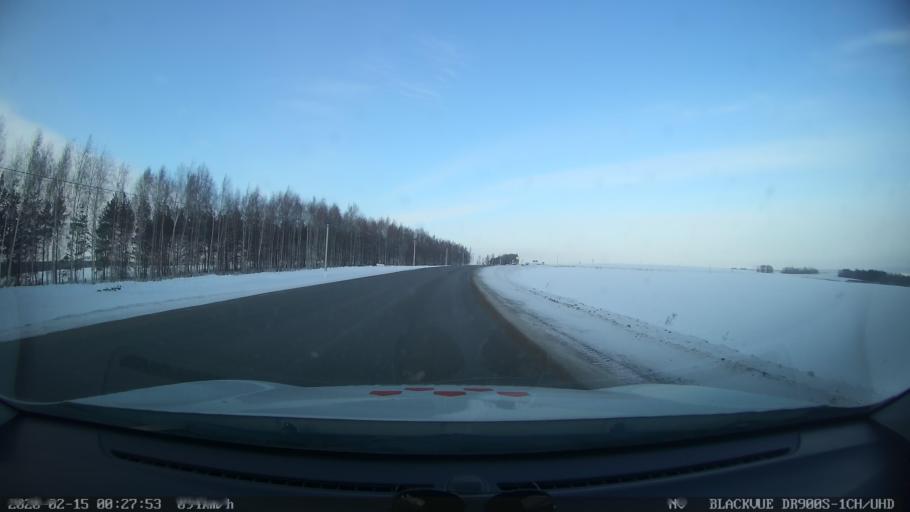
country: RU
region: Tatarstan
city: Verkhniy Uslon
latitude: 55.6348
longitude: 48.8713
